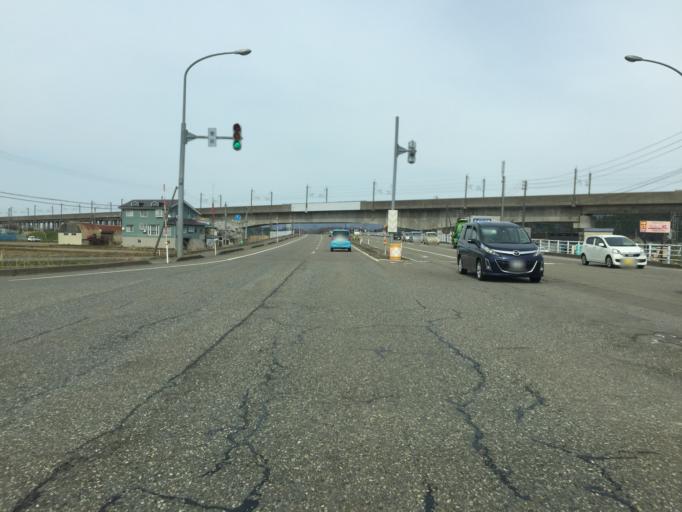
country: JP
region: Niigata
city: Nagaoka
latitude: 37.4009
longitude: 138.8448
